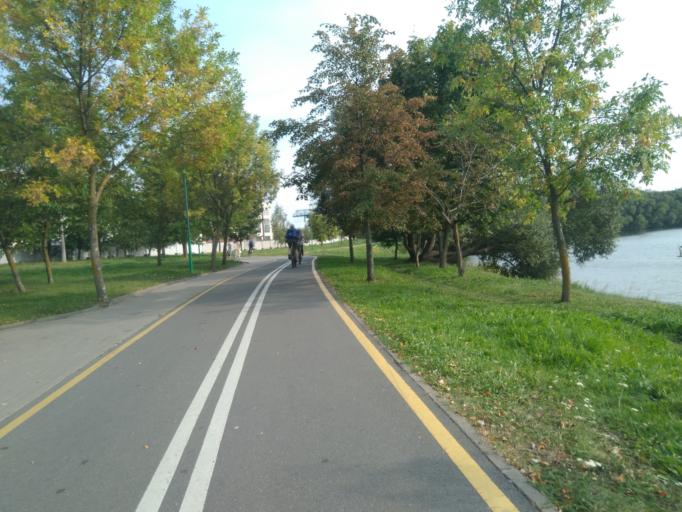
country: BY
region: Minsk
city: Minsk
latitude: 53.8825
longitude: 27.5741
